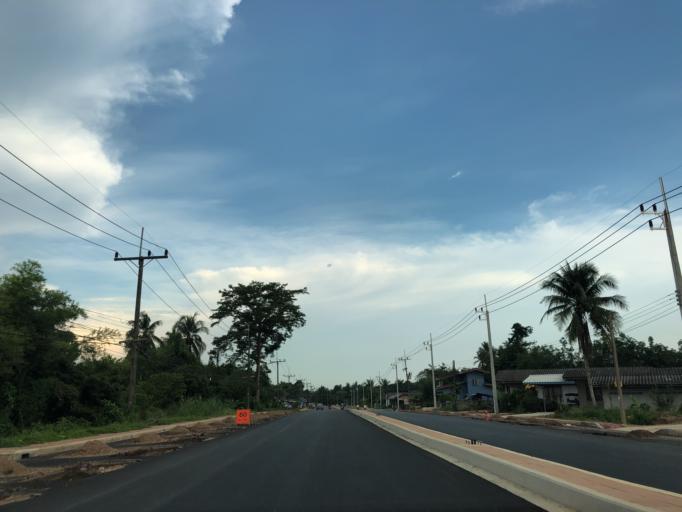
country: TH
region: Phangnga
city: Ban Ao Nang
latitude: 8.0690
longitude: 98.8416
